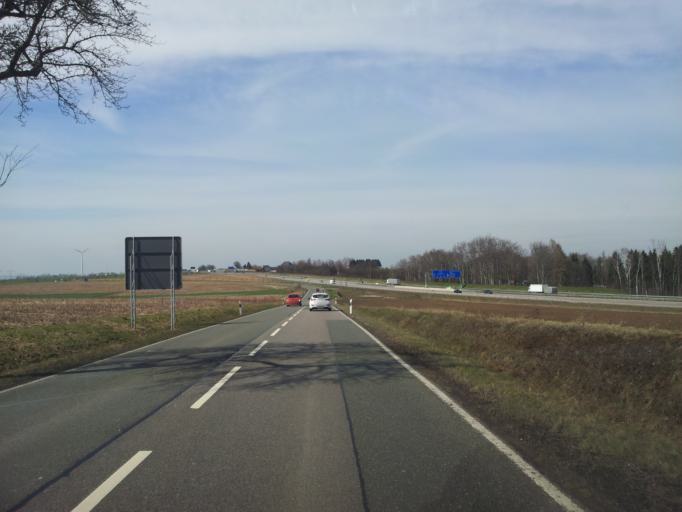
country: DE
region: Saxony
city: Callenberg
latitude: 50.8149
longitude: 12.6610
